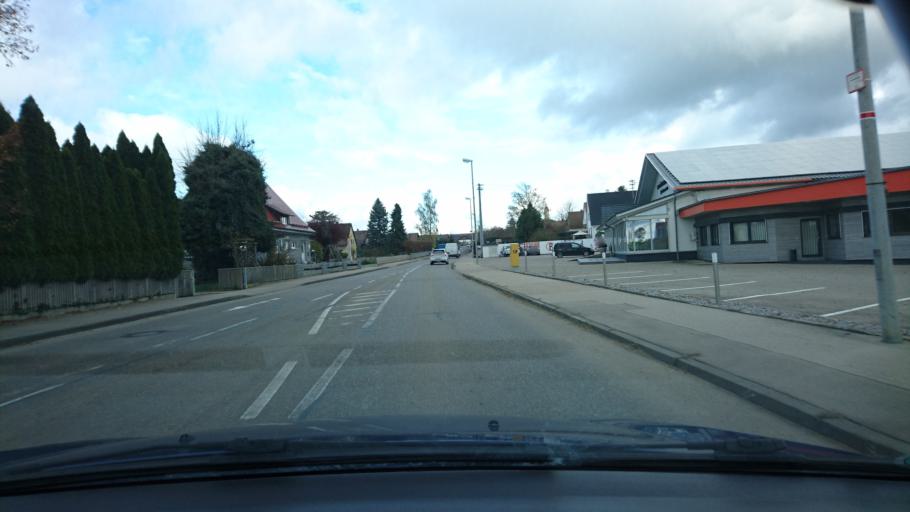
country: DE
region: Baden-Wuerttemberg
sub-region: Regierungsbezirk Stuttgart
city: Neresheim
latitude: 48.7881
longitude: 10.2669
